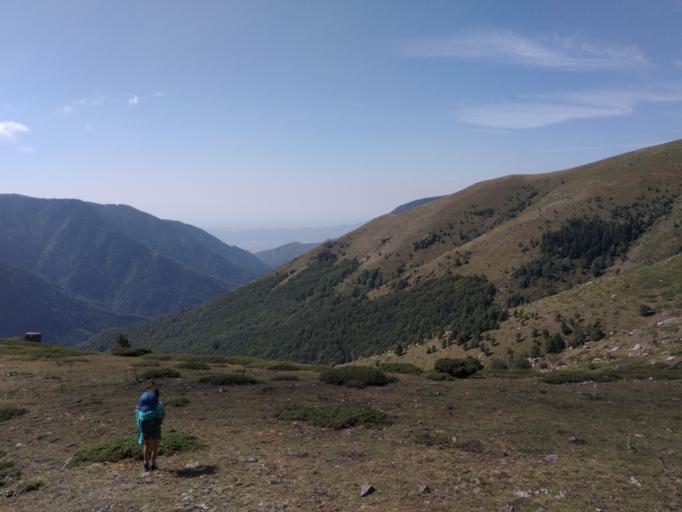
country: BG
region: Plovdiv
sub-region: Obshtina Karlovo
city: Karlovo
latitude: 42.7159
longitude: 24.8273
